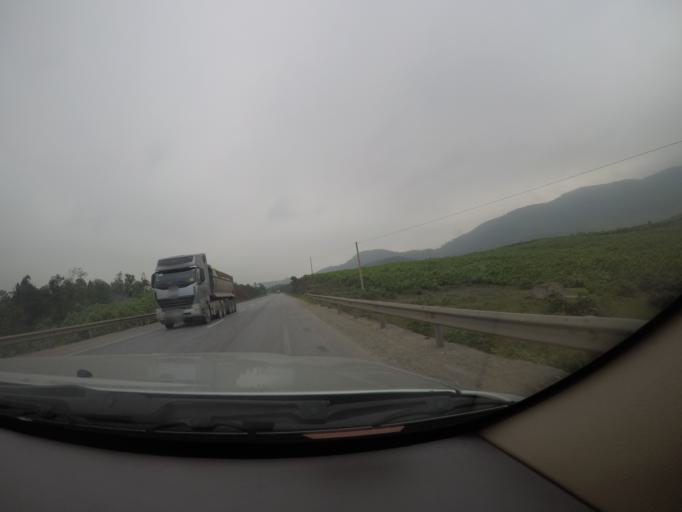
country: VN
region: Ha Tinh
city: Ky Anh
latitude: 18.0292
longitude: 106.3272
